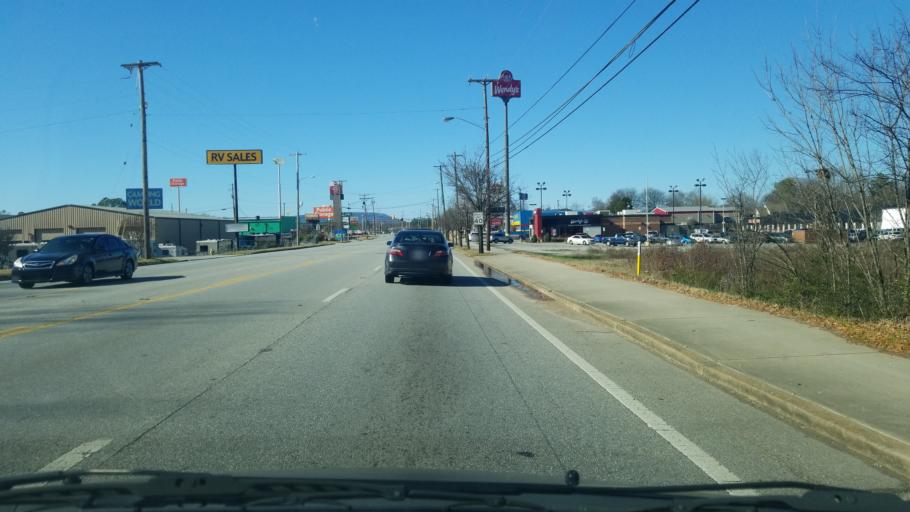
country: US
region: Georgia
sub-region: Catoosa County
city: Indian Springs
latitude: 34.9894
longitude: -85.1957
